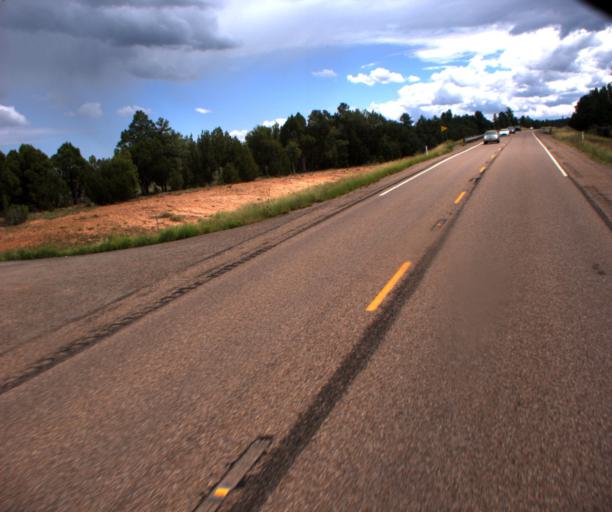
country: US
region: Arizona
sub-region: Navajo County
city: Linden
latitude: 34.3109
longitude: -110.2240
